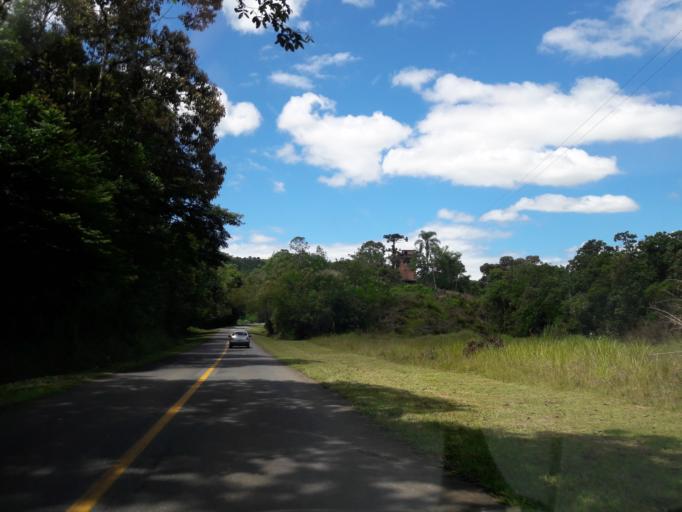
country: BR
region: Parana
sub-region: Antonina
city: Antonina
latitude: -25.4167
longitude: -48.8297
